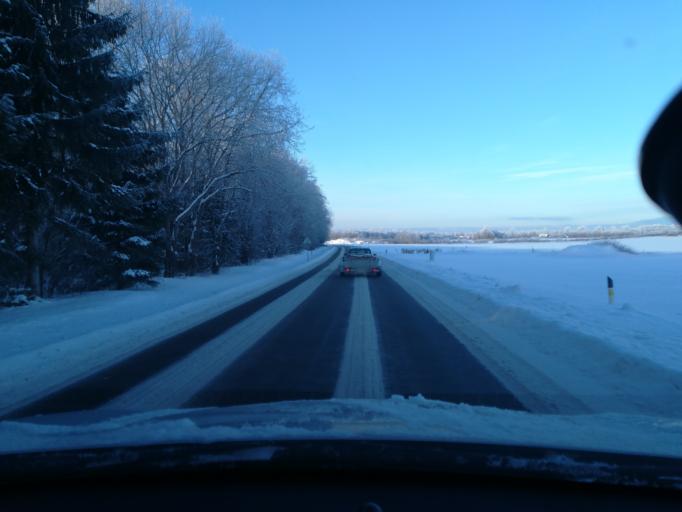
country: EE
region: Harju
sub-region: Saue linn
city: Saue
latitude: 59.3622
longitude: 24.5516
